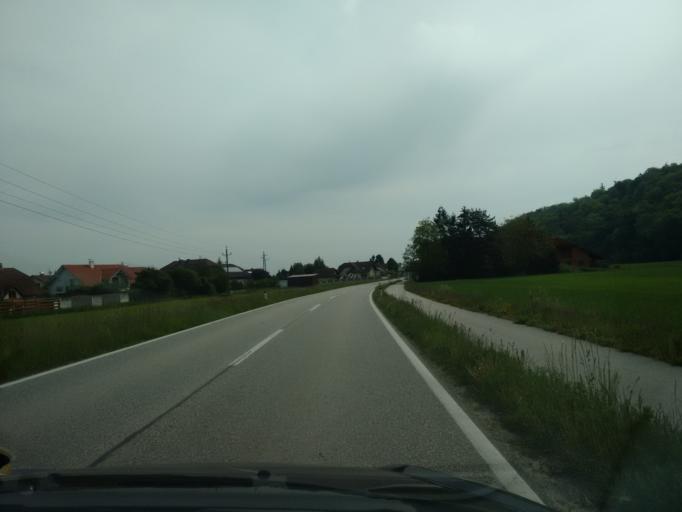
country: AT
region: Upper Austria
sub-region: Politischer Bezirk Linz-Land
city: Horsching
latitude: 48.1901
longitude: 14.1998
